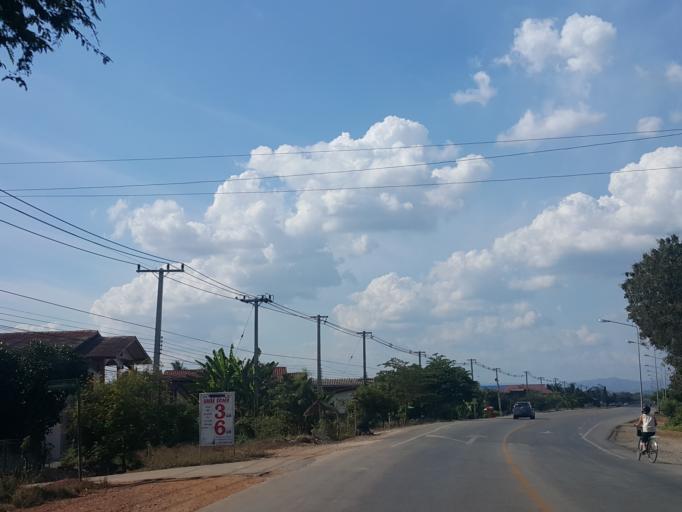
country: TH
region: Sukhothai
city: Thung Saliam
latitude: 17.3168
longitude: 99.6422
